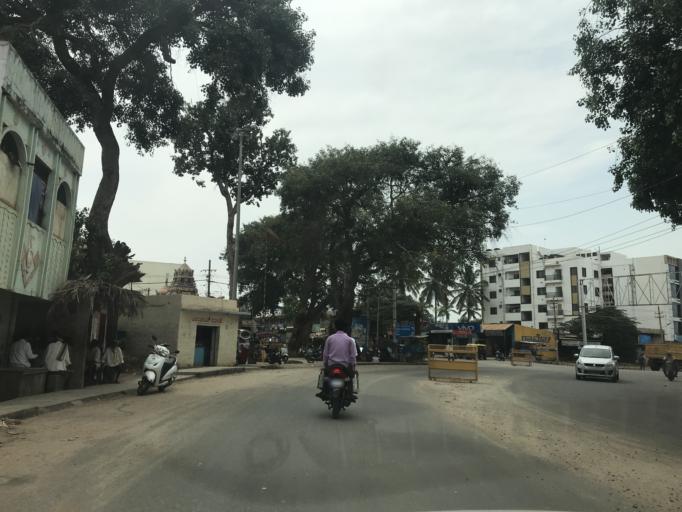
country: IN
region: Karnataka
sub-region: Bangalore Urban
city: Yelahanka
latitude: 13.0927
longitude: 77.6546
